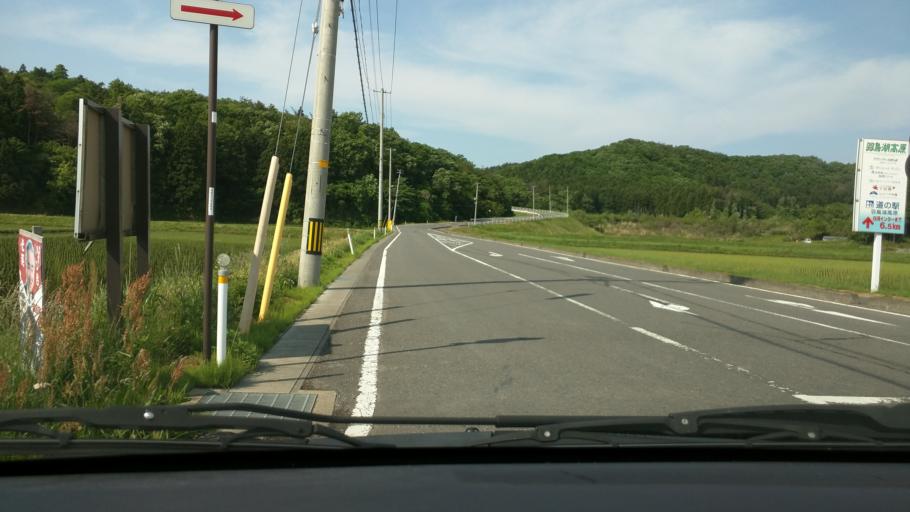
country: JP
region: Tochigi
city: Kuroiso
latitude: 37.1661
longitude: 140.1720
